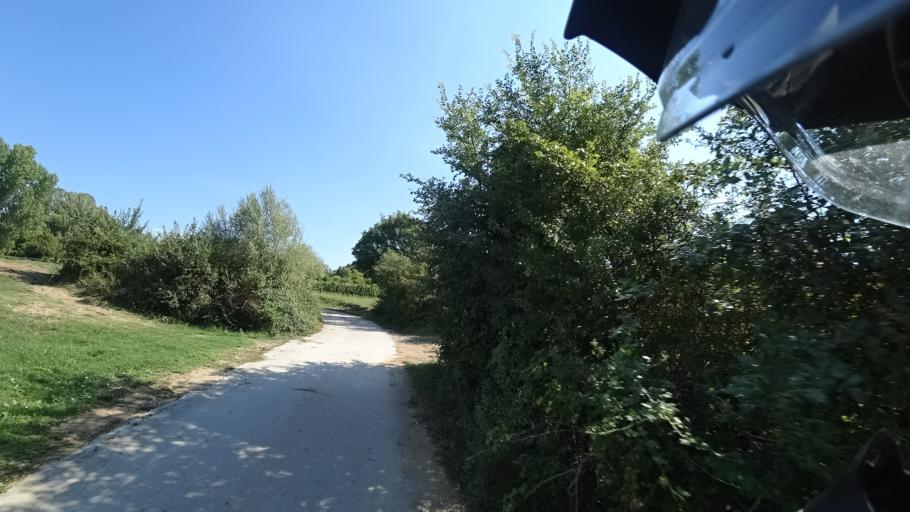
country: HR
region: Sibensko-Kniniska
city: Drnis
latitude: 43.8592
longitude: 16.2300
